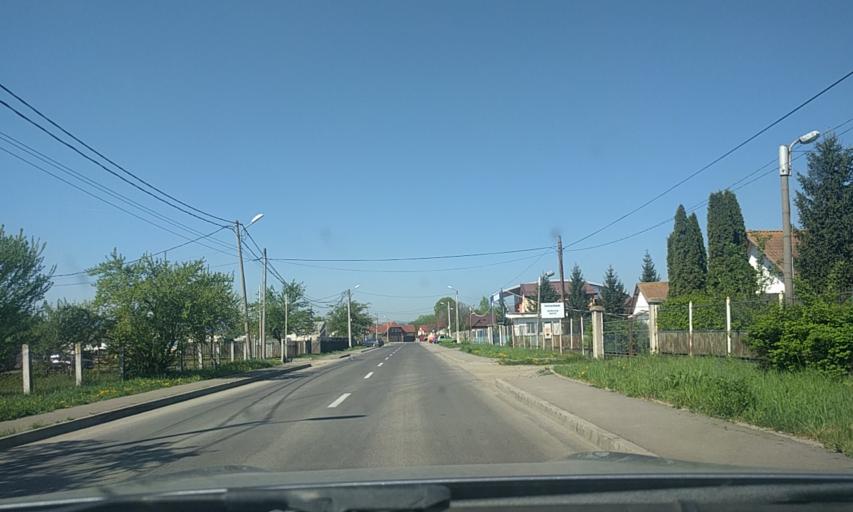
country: RO
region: Brasov
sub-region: Comuna Bod
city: Colonia Bod
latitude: 45.7080
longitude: 25.5780
